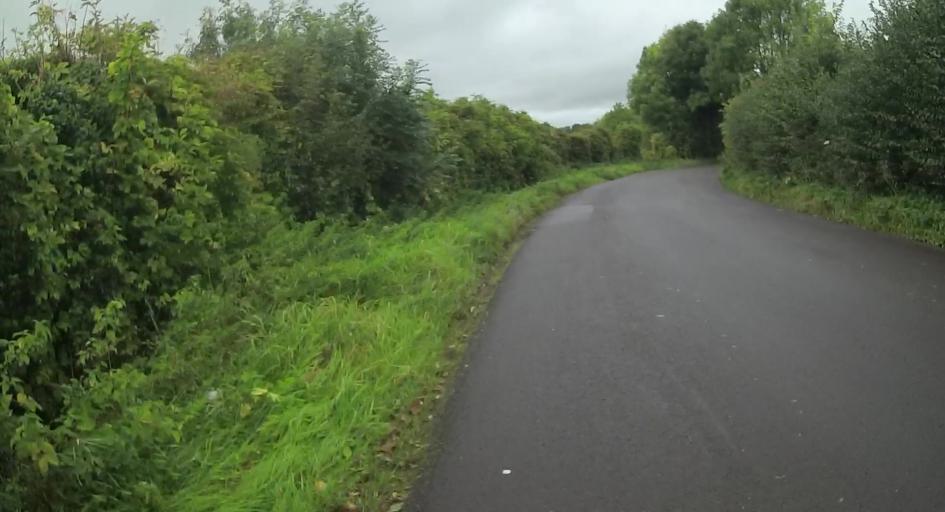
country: GB
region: England
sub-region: Hampshire
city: Tadley
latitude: 51.3910
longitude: -1.1778
